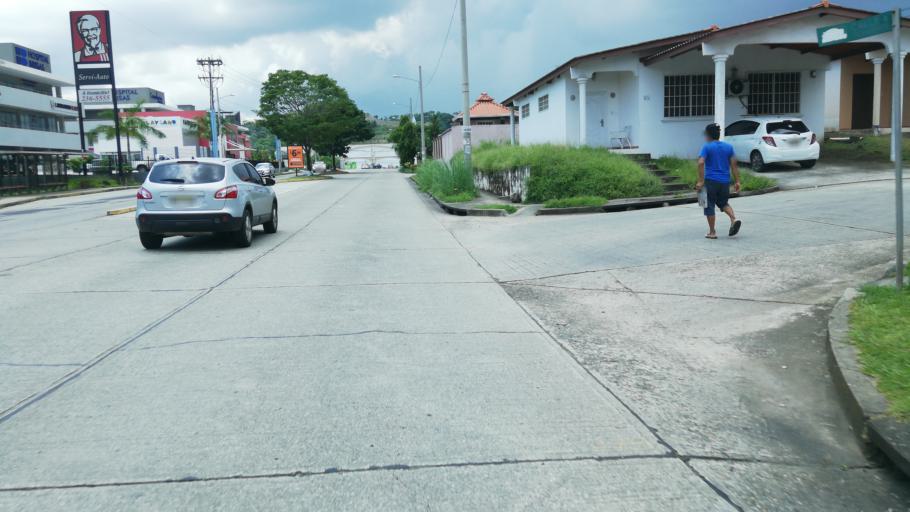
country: PA
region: Panama
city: San Miguelito
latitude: 9.0704
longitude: -79.4596
